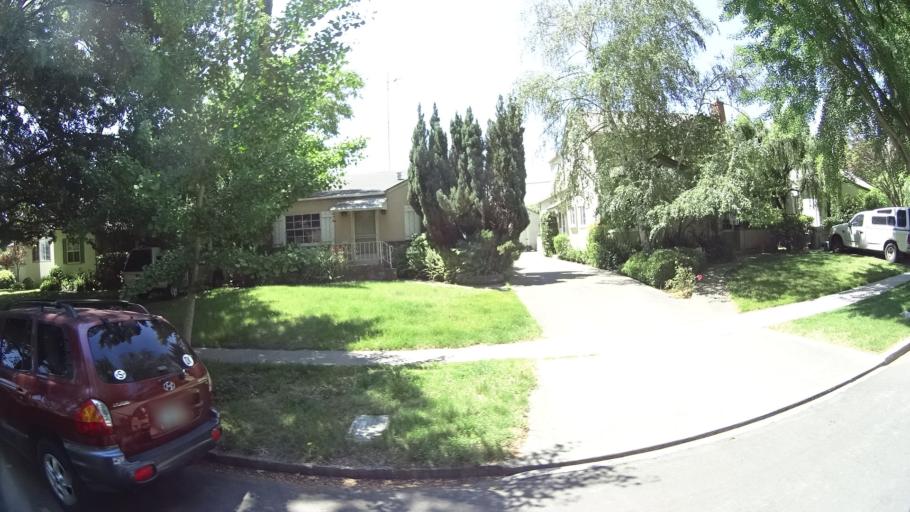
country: US
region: California
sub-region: Sacramento County
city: Sacramento
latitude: 38.5505
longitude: -121.4938
